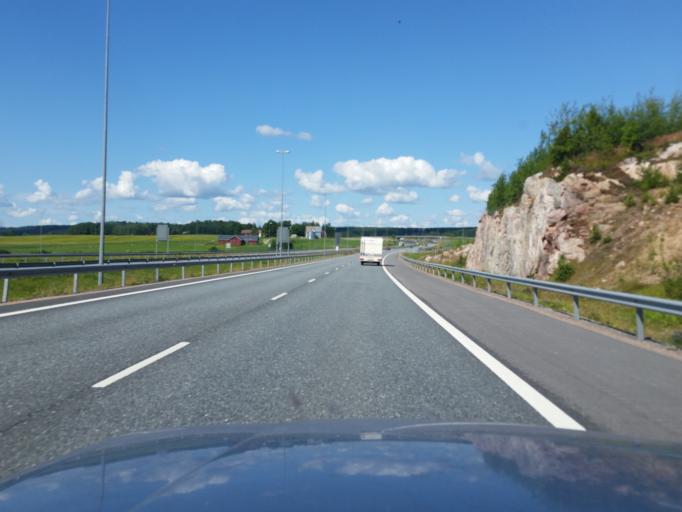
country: FI
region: Varsinais-Suomi
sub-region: Salo
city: Muurla
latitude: 60.3800
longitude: 23.3193
